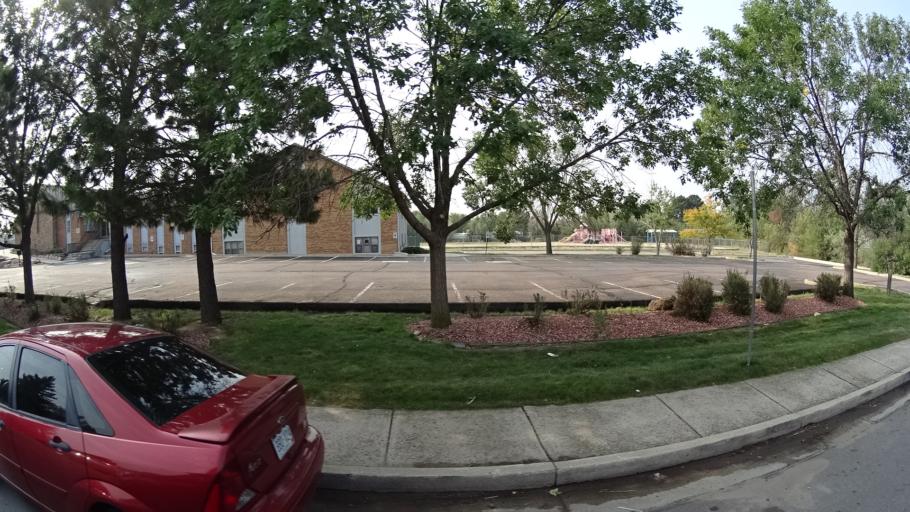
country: US
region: Colorado
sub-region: El Paso County
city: Stratmoor
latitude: 38.8008
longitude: -104.7601
